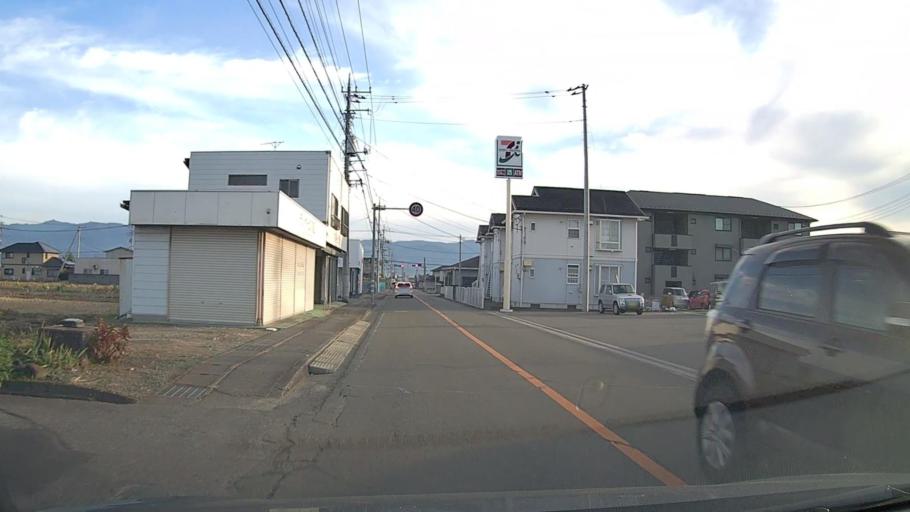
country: JP
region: Yamanashi
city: Ryuo
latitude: 35.6345
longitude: 138.5218
